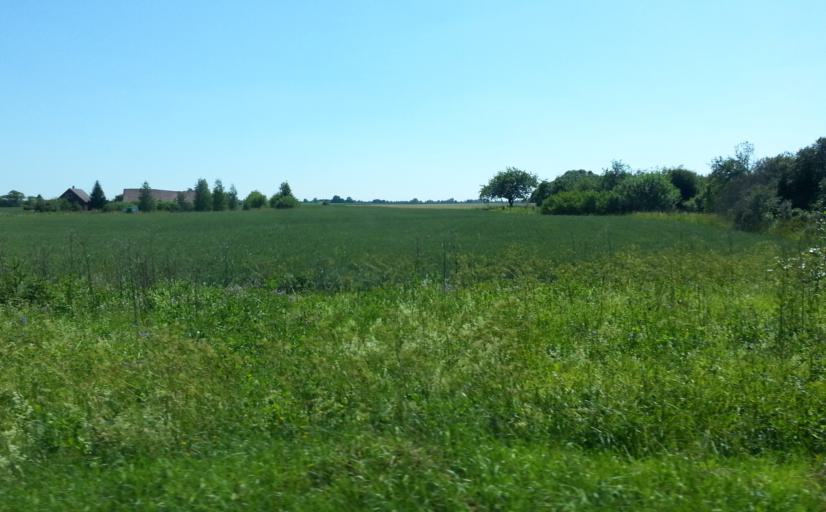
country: LT
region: Panevezys
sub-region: Birzai
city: Birzai
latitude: 56.2129
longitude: 24.6734
